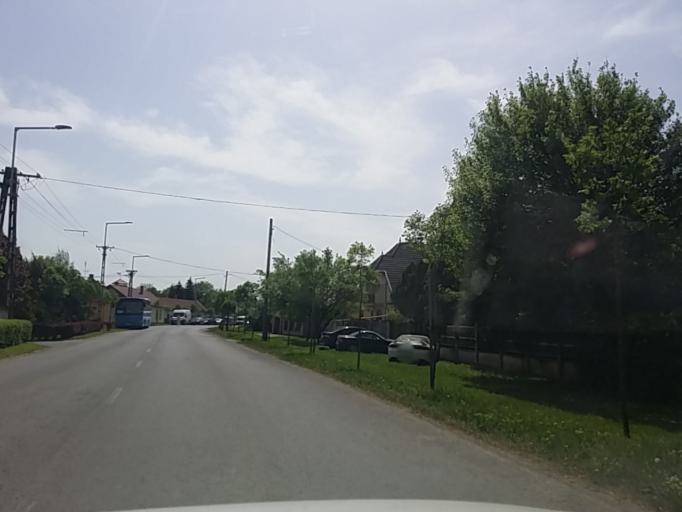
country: HU
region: Bekes
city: Gyula
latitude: 46.6495
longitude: 21.2836
